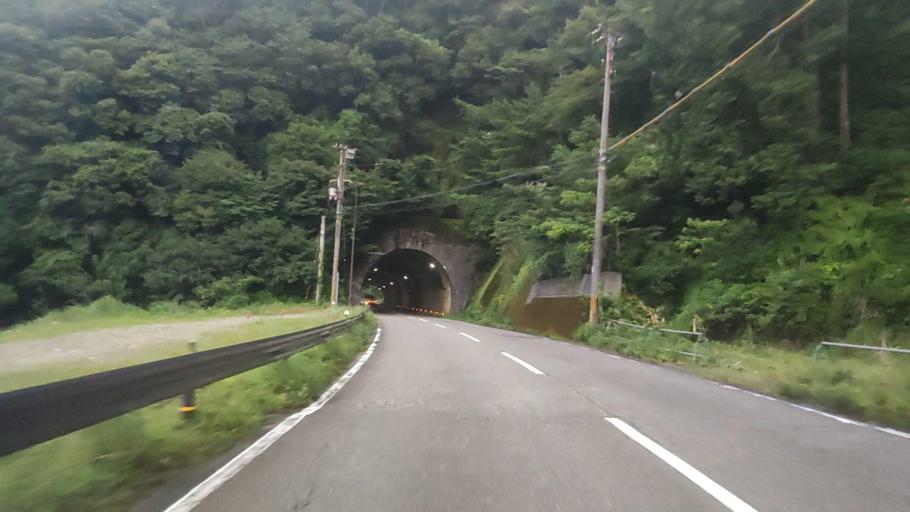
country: JP
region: Wakayama
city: Shingu
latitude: 33.7569
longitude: 135.9209
